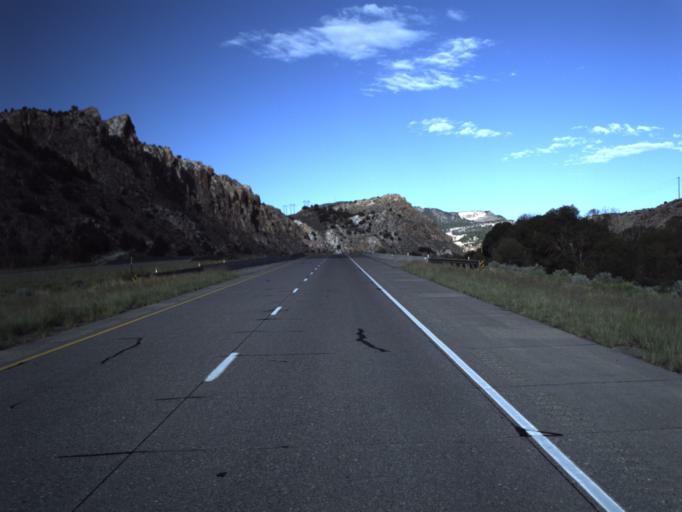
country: US
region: Utah
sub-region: Sevier County
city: Monroe
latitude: 38.5787
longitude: -112.3132
